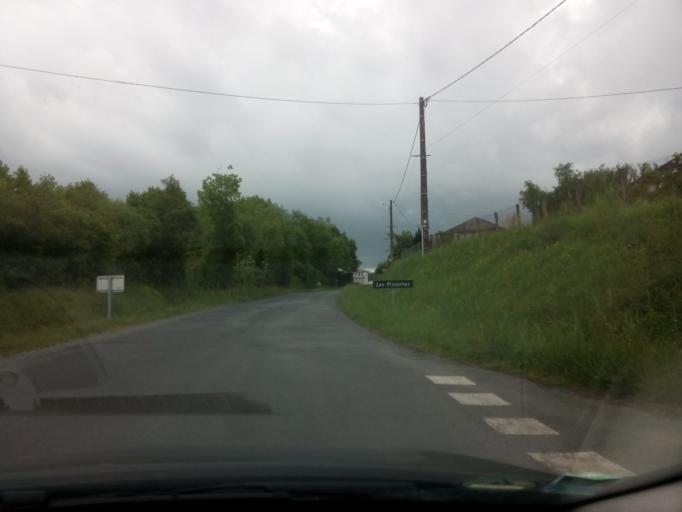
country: FR
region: Limousin
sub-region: Departement de la Correze
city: Allassac
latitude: 45.2661
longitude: 1.4660
